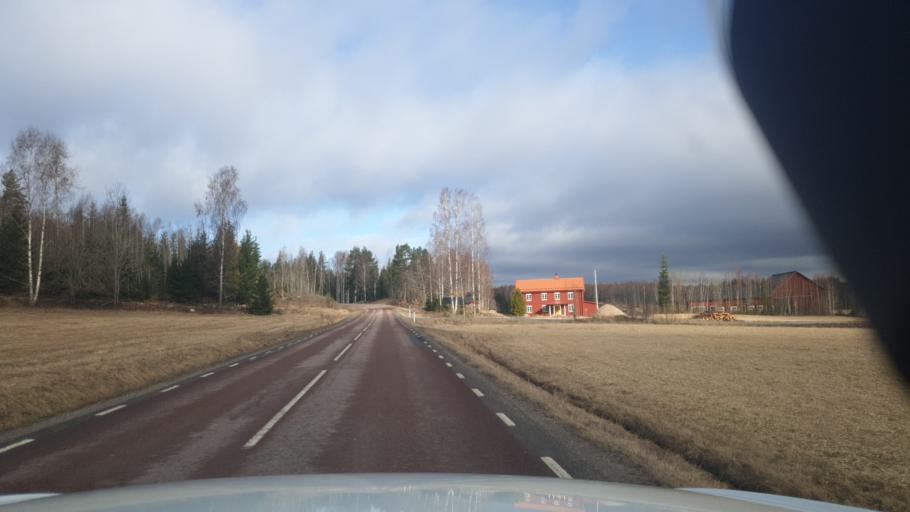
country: SE
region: Vaermland
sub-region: Grums Kommun
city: Grums
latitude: 59.4557
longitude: 12.9670
